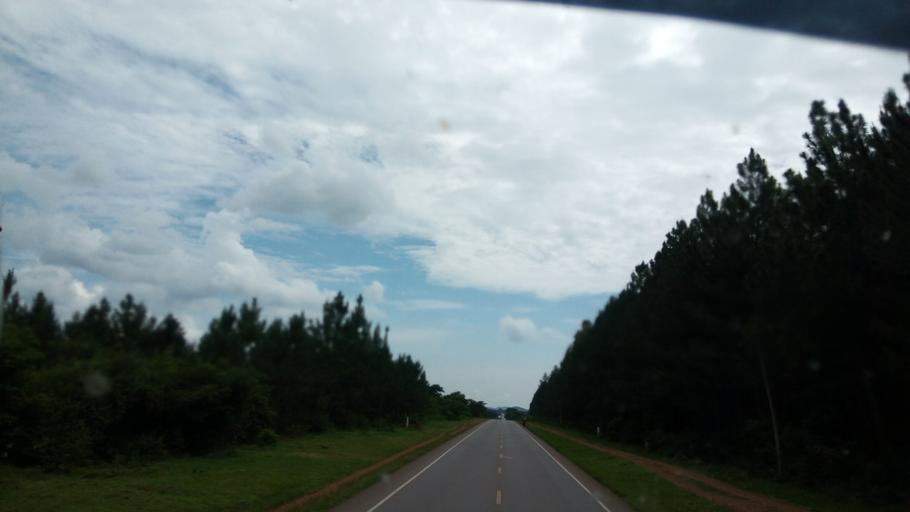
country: UG
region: Central Region
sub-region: Nakasongola District
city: Nakasongola
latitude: 1.1917
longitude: 32.4613
